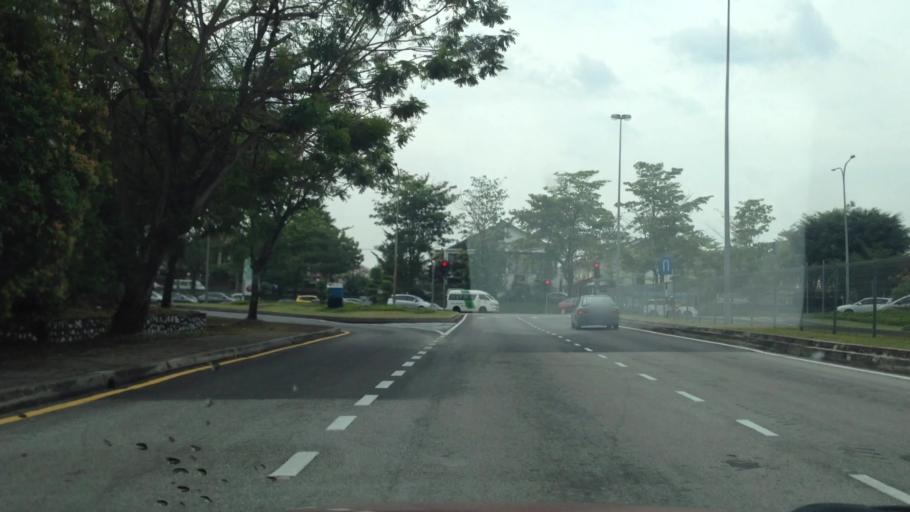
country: MY
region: Selangor
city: Subang Jaya
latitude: 3.0450
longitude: 101.5751
